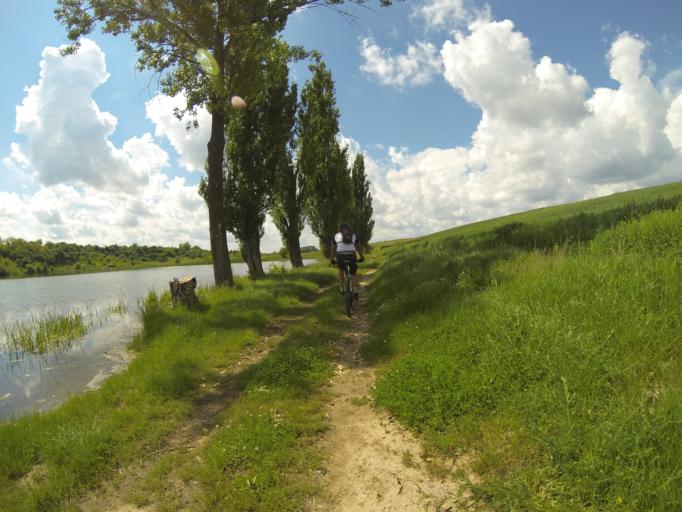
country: RO
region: Dolj
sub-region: Comuna Malu Mare
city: Preajba
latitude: 44.2671
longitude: 23.8533
